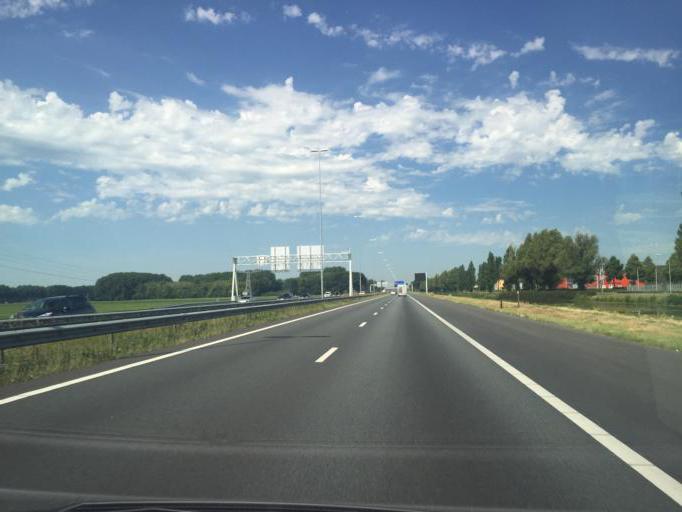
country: NL
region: Gelderland
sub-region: Gemeente Beuningen
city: Beuningen
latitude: 51.8526
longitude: 5.7405
